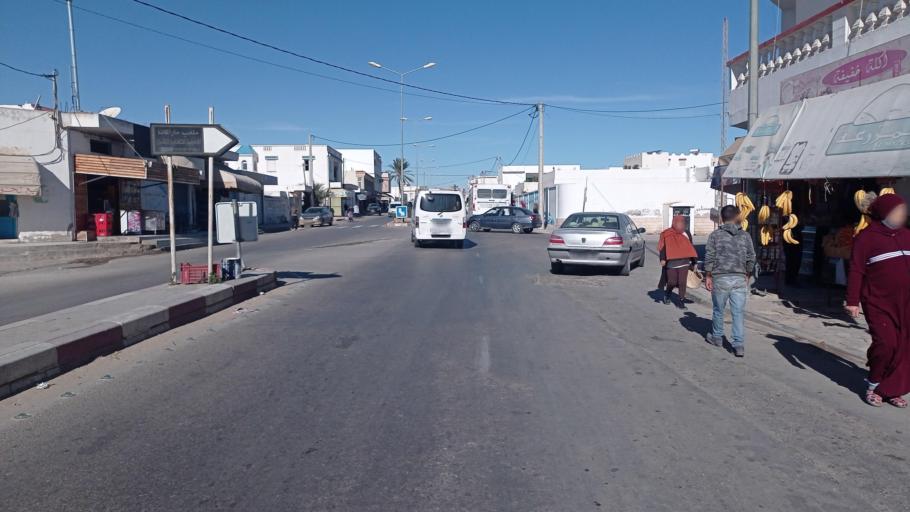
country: TN
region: Qabis
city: Gabes
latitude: 33.8395
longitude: 10.1156
